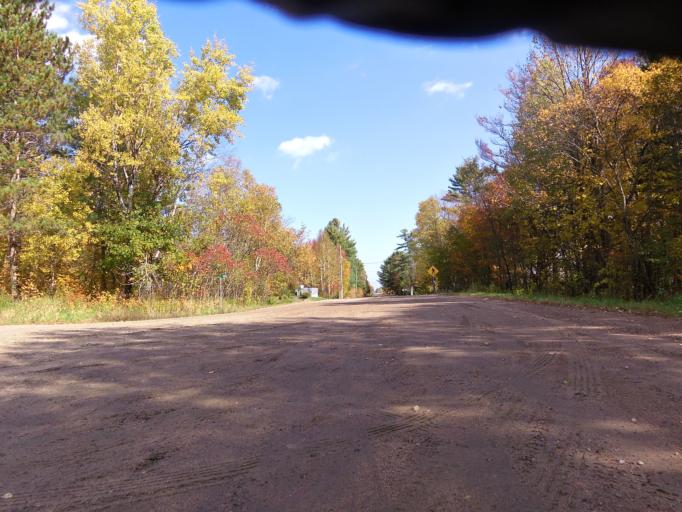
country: CA
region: Ontario
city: Petawawa
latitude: 45.8085
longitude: -77.2772
